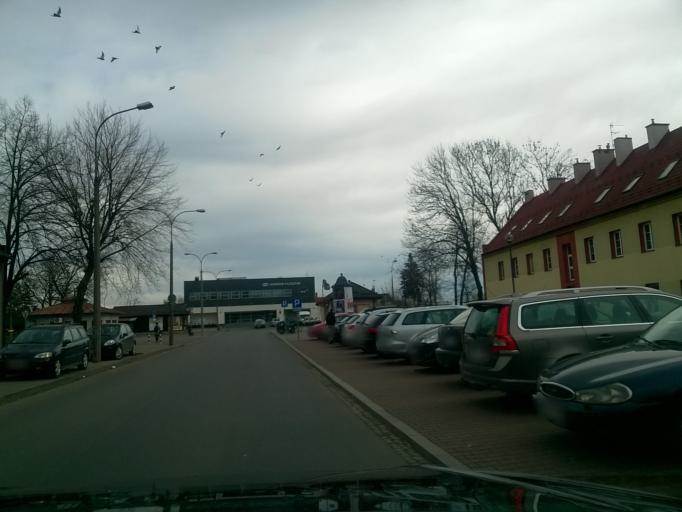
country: PL
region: Lesser Poland Voivodeship
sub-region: Krakow
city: Krakow
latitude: 50.0341
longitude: 19.9733
